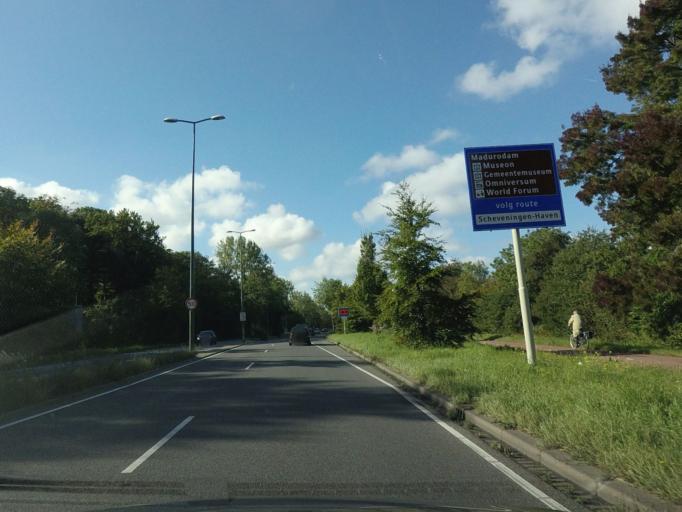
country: NL
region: South Holland
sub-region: Gemeente Leidschendam-Voorburg
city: Voorburg
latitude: 52.0971
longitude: 4.3416
